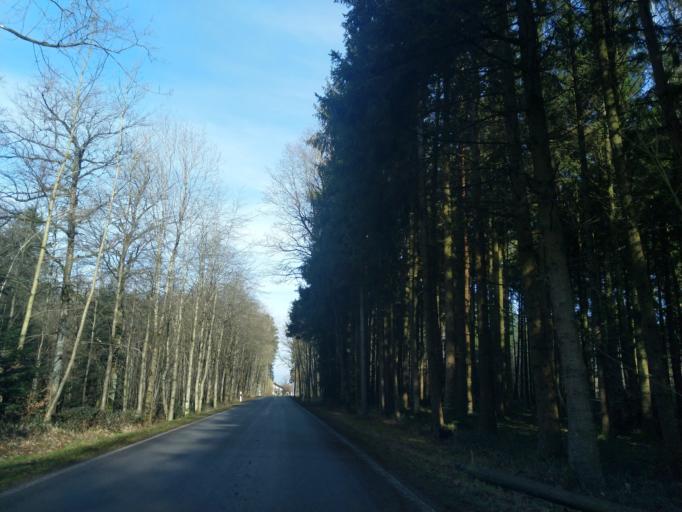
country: DE
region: Bavaria
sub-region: Lower Bavaria
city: Buchhofen
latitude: 48.6648
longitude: 12.9187
